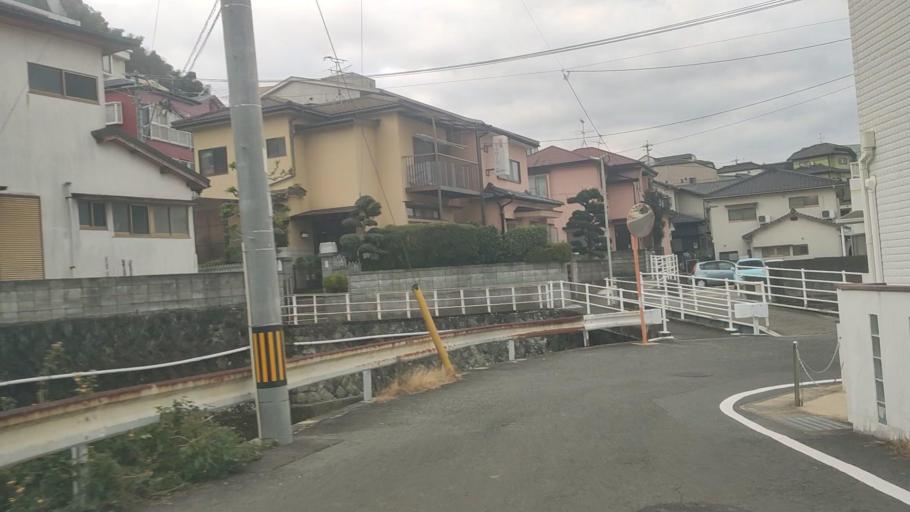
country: JP
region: Nagasaki
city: Nagasaki-shi
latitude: 32.7775
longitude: 129.8702
